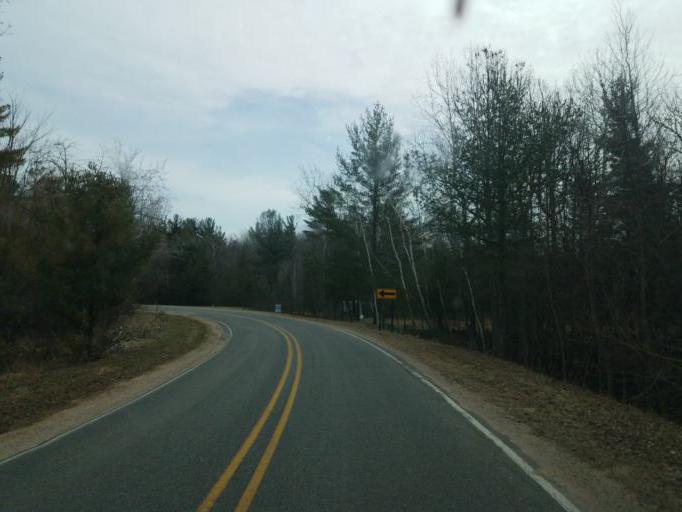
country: US
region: Michigan
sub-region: Oceana County
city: Hart
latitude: 43.7331
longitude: -86.4607
